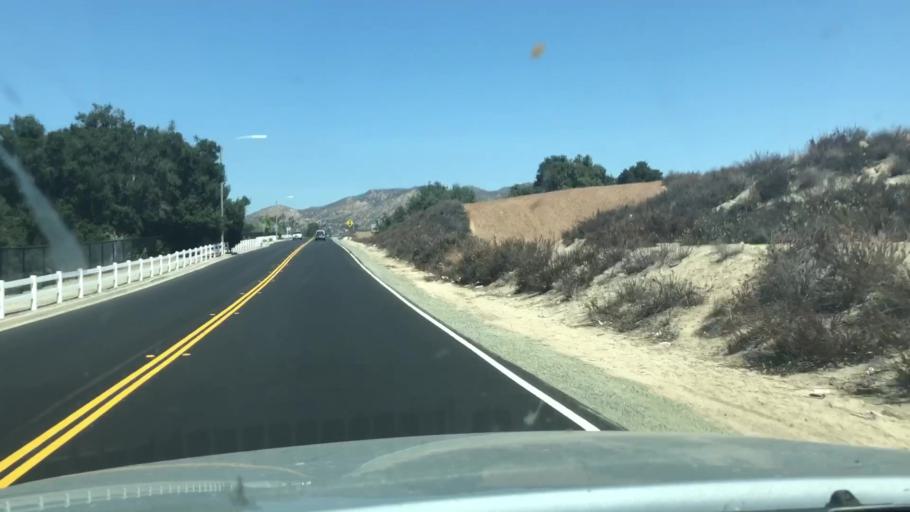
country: US
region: California
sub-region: Riverside County
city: Wildomar
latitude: 33.5945
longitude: -117.2368
